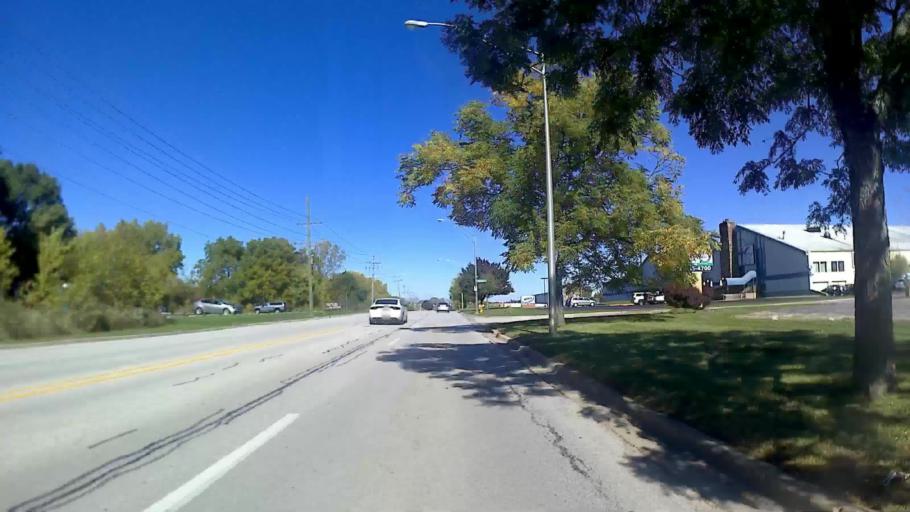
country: US
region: Illinois
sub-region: DuPage County
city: Addison
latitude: 41.9162
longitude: -88.0081
